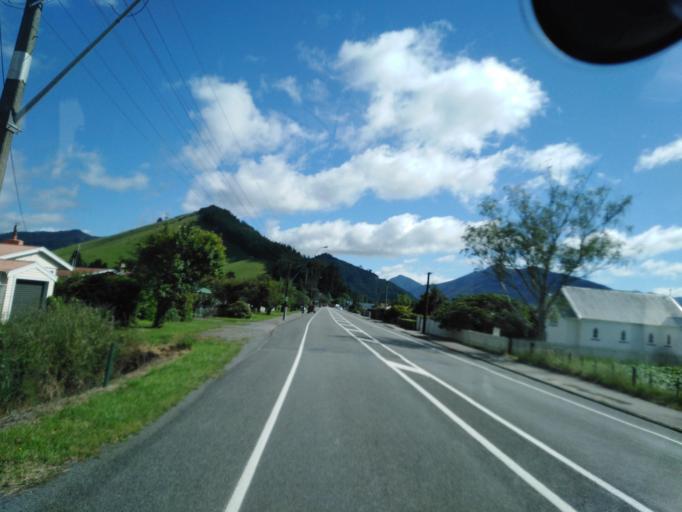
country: NZ
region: Nelson
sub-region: Nelson City
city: Nelson
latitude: -41.2309
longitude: 173.5820
